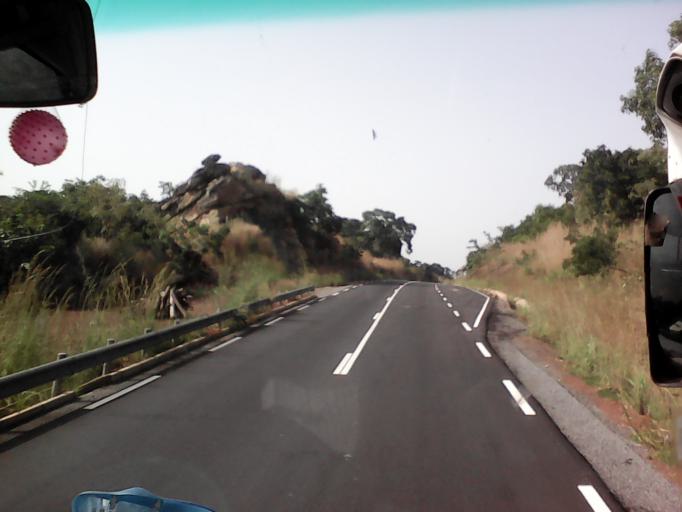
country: TG
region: Kara
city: Bafilo
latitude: 9.2447
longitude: 1.2141
